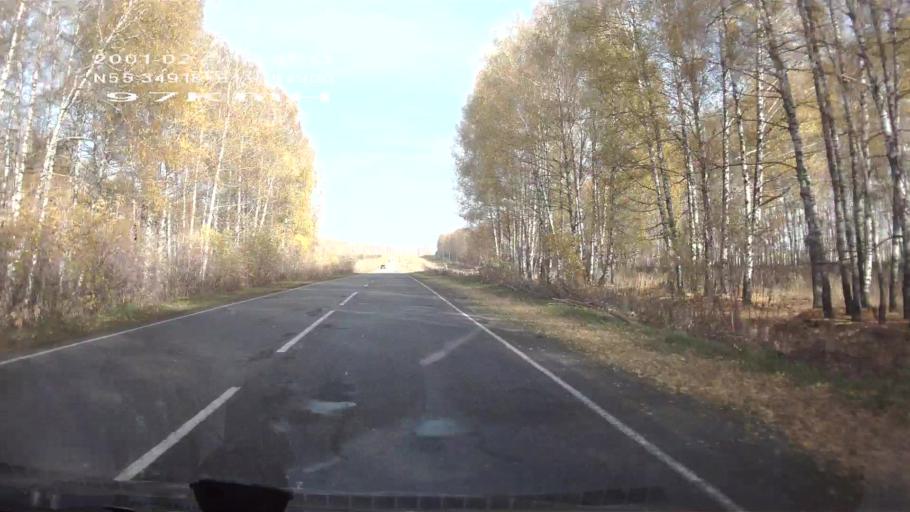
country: RU
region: Chuvashia
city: Ibresi
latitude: 55.3492
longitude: 47.1873
